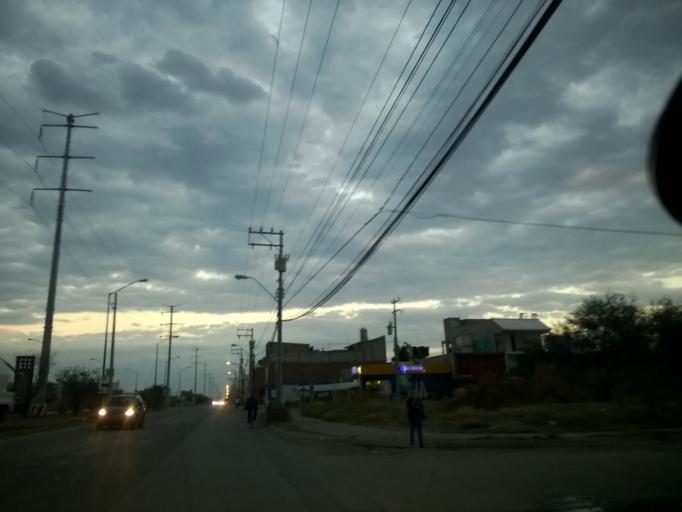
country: MX
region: Guanajuato
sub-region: Leon
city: Fraccionamiento Paraiso Real
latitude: 21.0757
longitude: -101.6167
